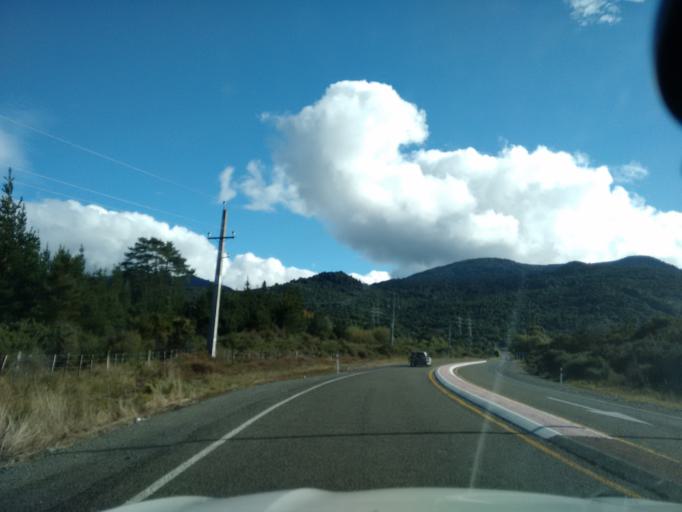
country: NZ
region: Waikato
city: Turangi
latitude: -38.9821
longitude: 175.7791
